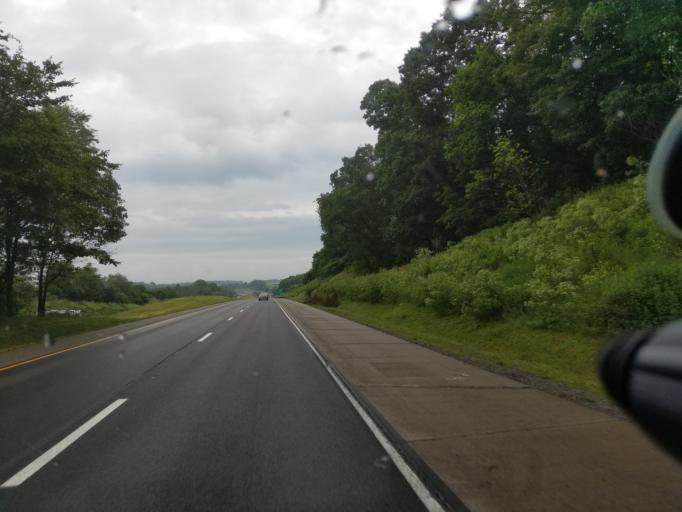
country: US
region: Pennsylvania
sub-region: Northumberland County
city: Milton
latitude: 41.0310
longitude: -76.8049
